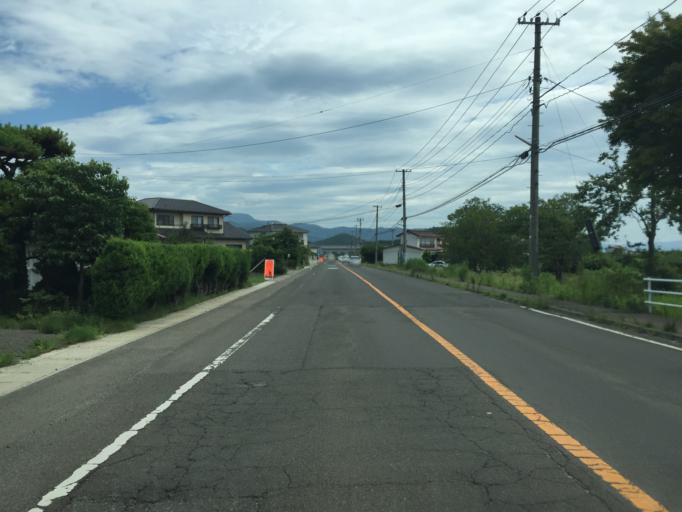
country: JP
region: Fukushima
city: Fukushima-shi
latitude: 37.8017
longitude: 140.4059
